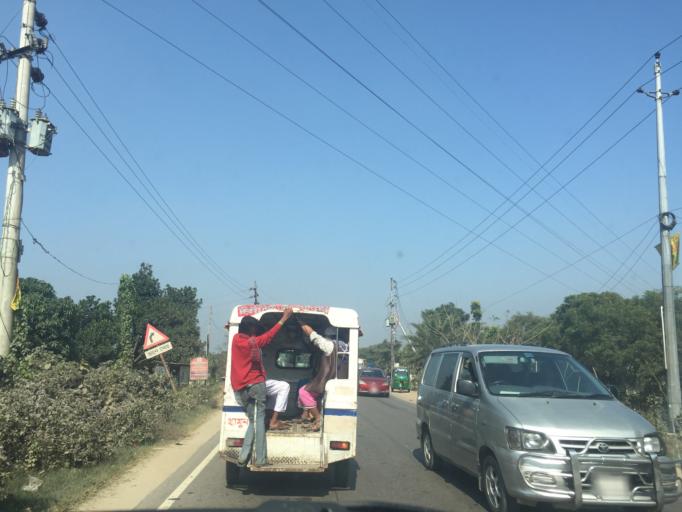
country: BD
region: Dhaka
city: Tungi
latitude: 23.8199
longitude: 90.3416
